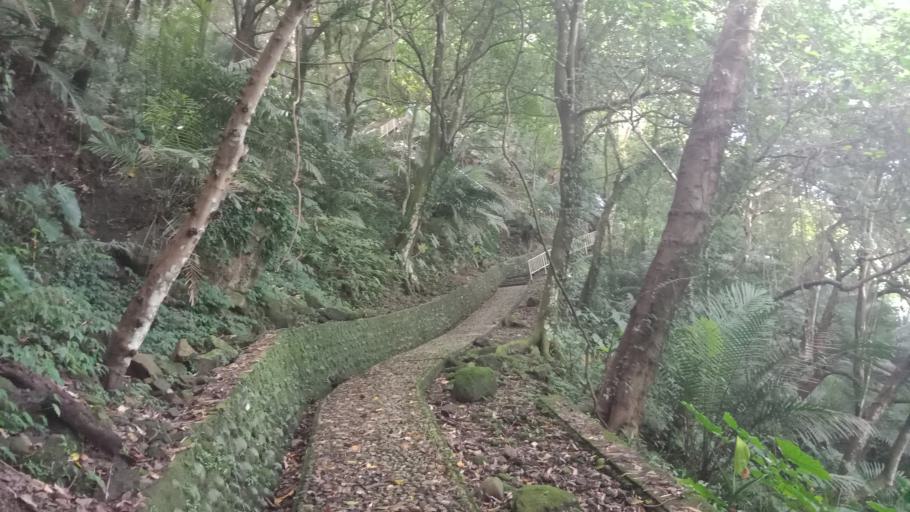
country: TW
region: Taiwan
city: Daxi
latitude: 24.8140
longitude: 121.2491
